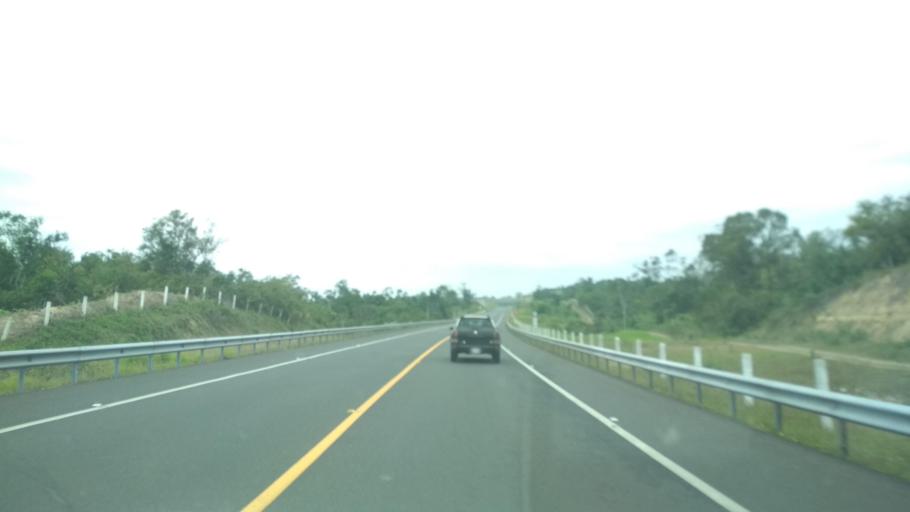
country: MX
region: Veracruz
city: Papantla de Olarte
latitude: 20.4360
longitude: -97.2321
